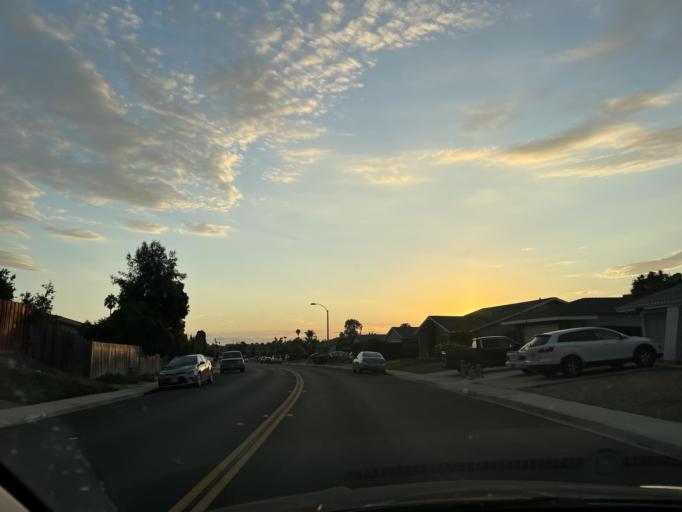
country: US
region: California
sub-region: San Diego County
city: Fairbanks Ranch
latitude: 32.9076
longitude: -117.1485
